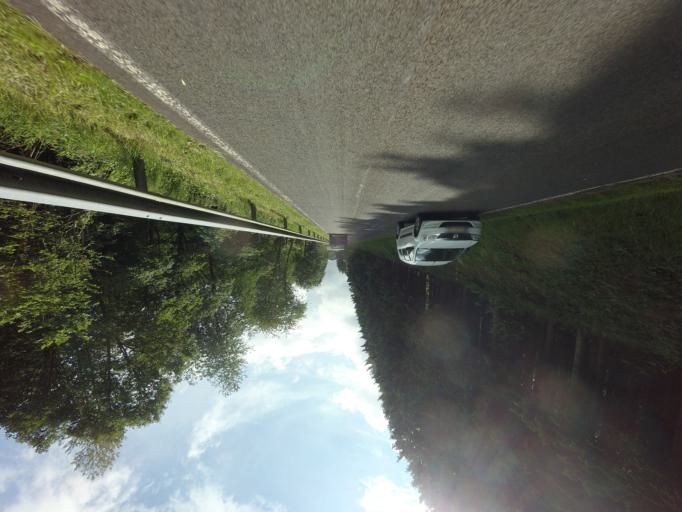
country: DE
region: Rheinland-Pfalz
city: Welschenbach
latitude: 50.3671
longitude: 7.0684
